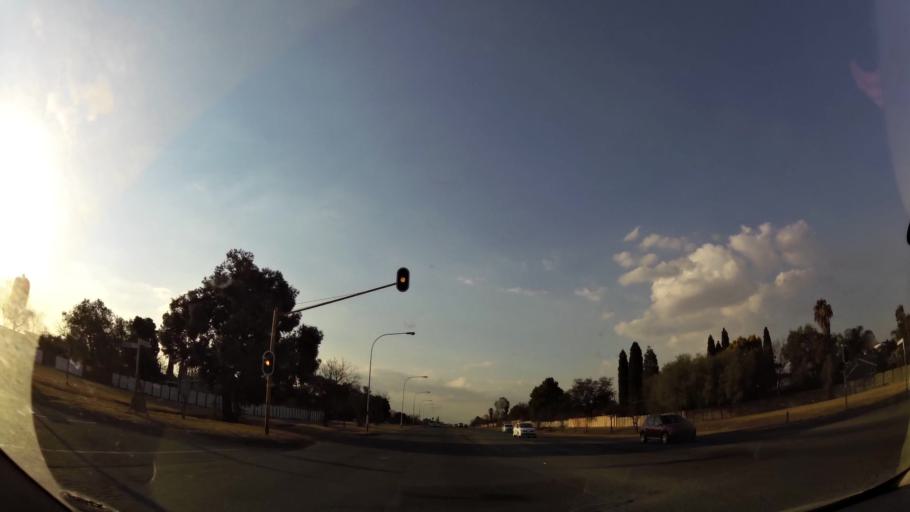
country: ZA
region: Gauteng
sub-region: Ekurhuleni Metropolitan Municipality
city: Boksburg
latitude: -26.2666
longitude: 28.2412
